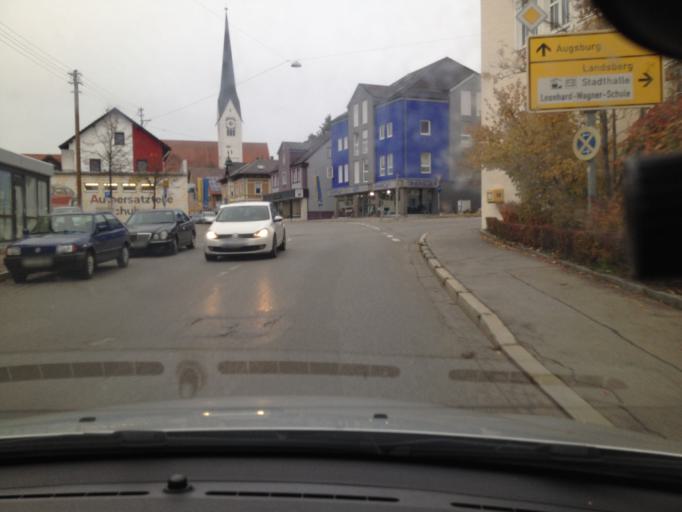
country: DE
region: Bavaria
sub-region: Swabia
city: Schwabmunchen
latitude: 48.1765
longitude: 10.7578
